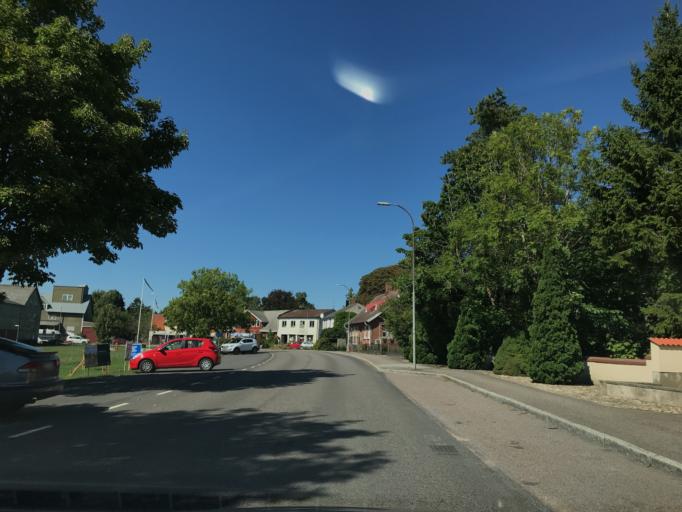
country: SE
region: Skane
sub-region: Tomelilla Kommun
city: Tomelilla
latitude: 55.6545
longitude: 13.8913
